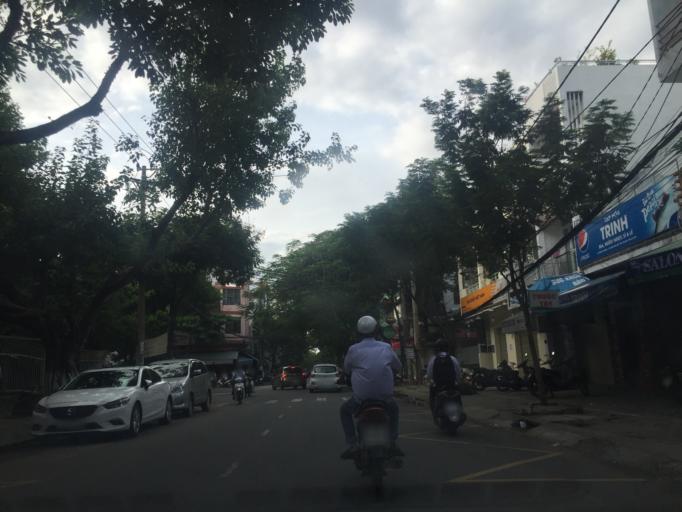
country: VN
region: Da Nang
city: Da Nang
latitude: 16.0780
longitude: 108.2119
